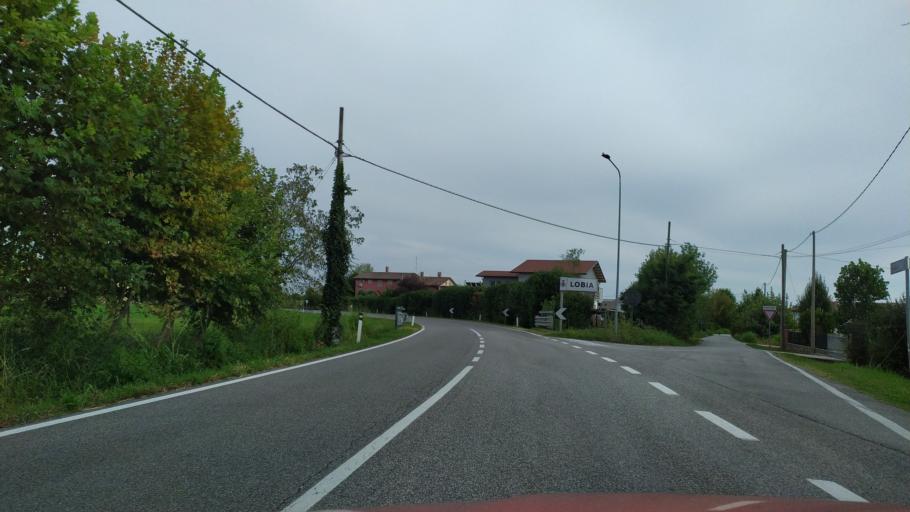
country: IT
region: Veneto
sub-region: Provincia di Padova
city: San Giorgio in Bosco
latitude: 45.5813
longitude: 11.7817
